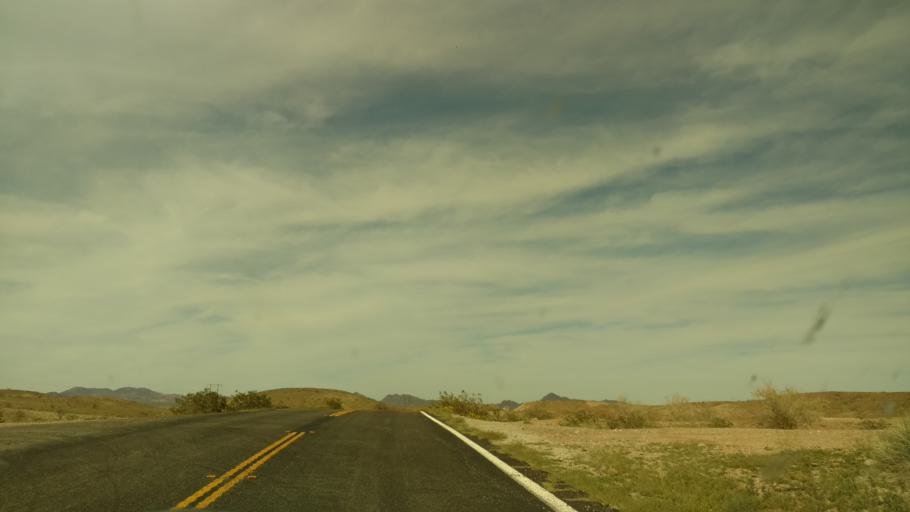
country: US
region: California
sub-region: Riverside County
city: Mesa Verde
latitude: 33.2184
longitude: -114.8537
